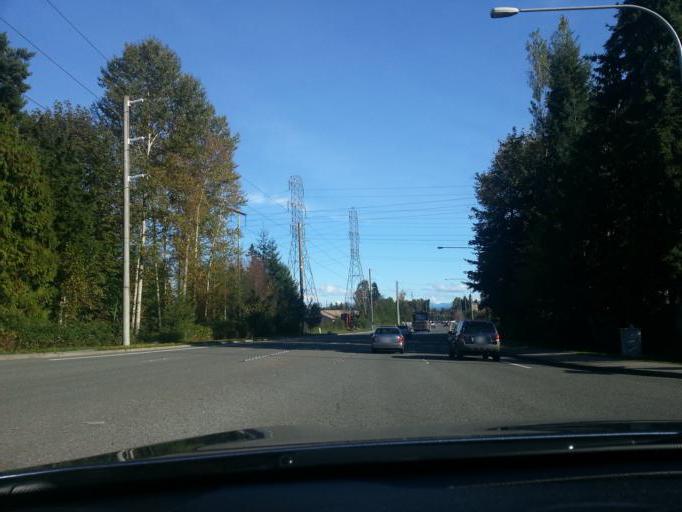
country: US
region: Washington
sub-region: Snohomish County
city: Silver Firs
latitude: 47.8776
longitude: -122.1587
